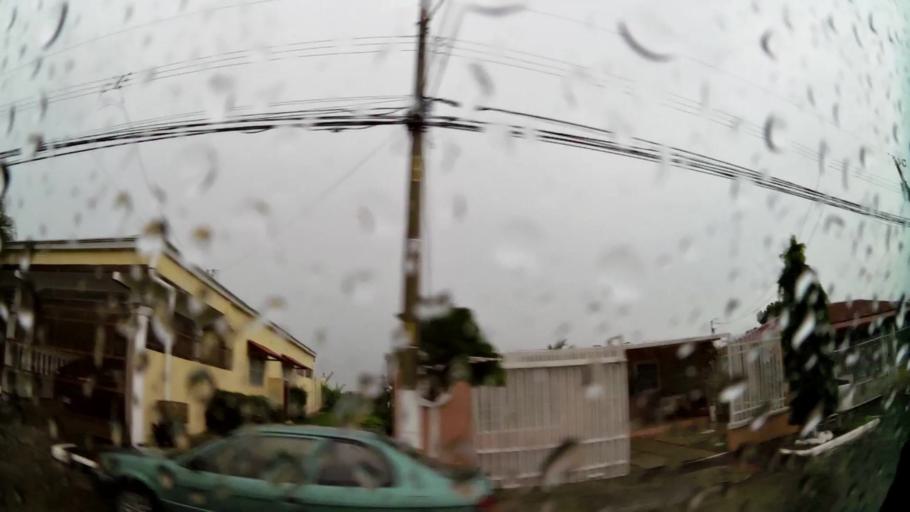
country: PA
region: Panama
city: San Miguelito
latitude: 9.0578
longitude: -79.4760
